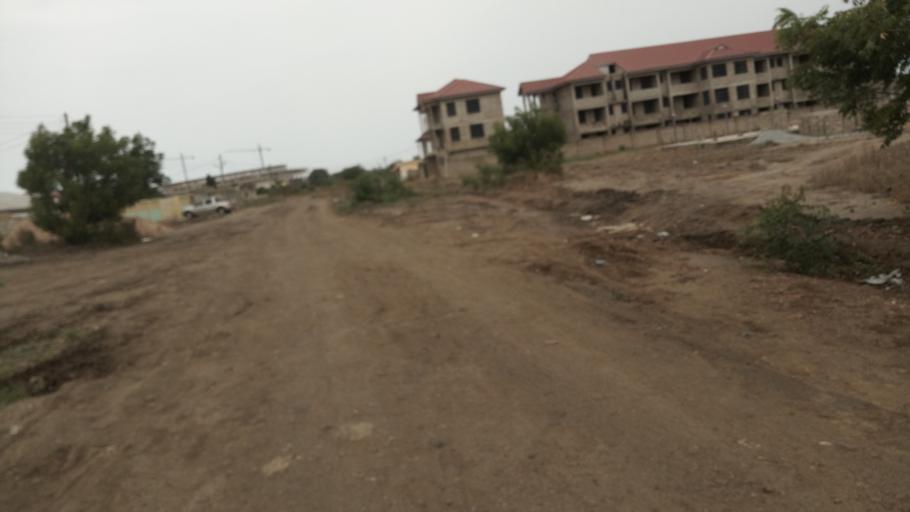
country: GH
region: Central
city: Winneba
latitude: 5.3760
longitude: -0.6335
